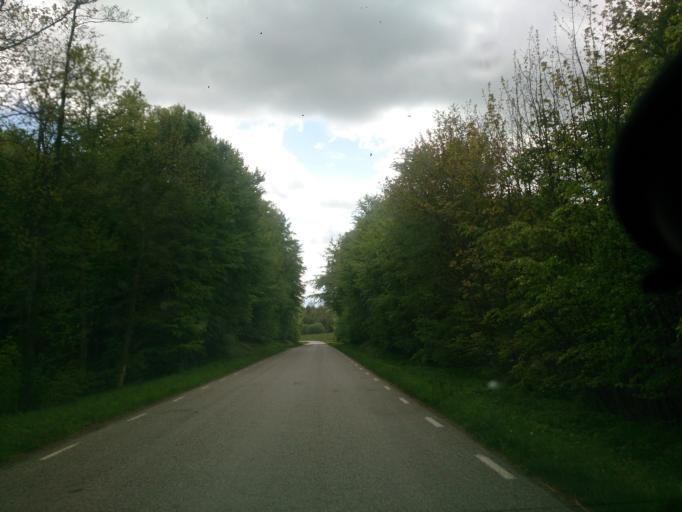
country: SE
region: Skane
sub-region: Sjobo Kommun
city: Sjoebo
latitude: 55.5510
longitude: 13.7117
